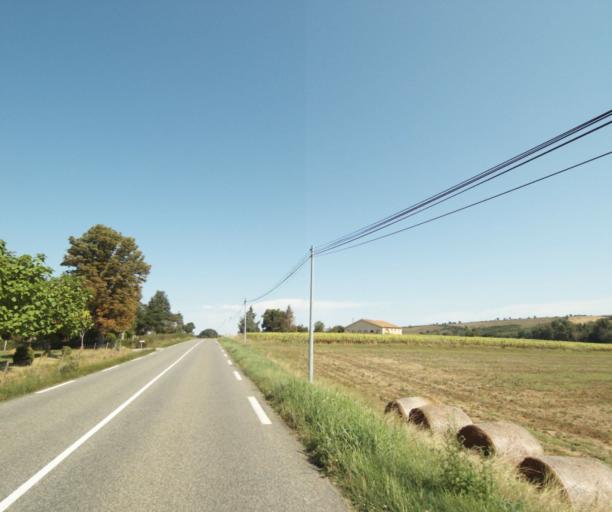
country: FR
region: Midi-Pyrenees
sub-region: Departement de l'Ariege
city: Lezat-sur-Leze
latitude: 43.2925
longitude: 1.3418
